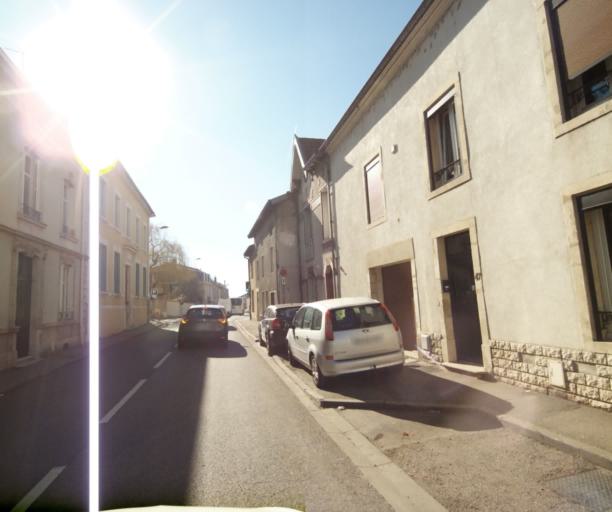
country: FR
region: Lorraine
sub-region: Departement de Meurthe-et-Moselle
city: Malzeville
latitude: 48.7114
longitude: 6.1843
